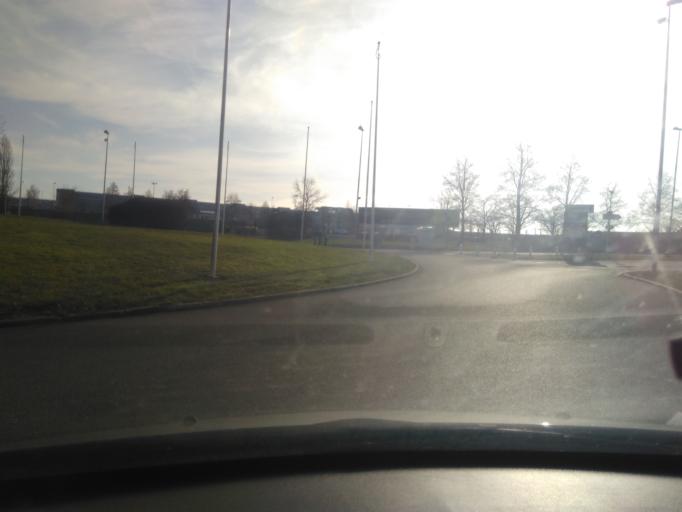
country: FR
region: Bourgogne
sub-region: Departement de la Nievre
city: Magny-Cours
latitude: 46.8675
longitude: 3.1598
